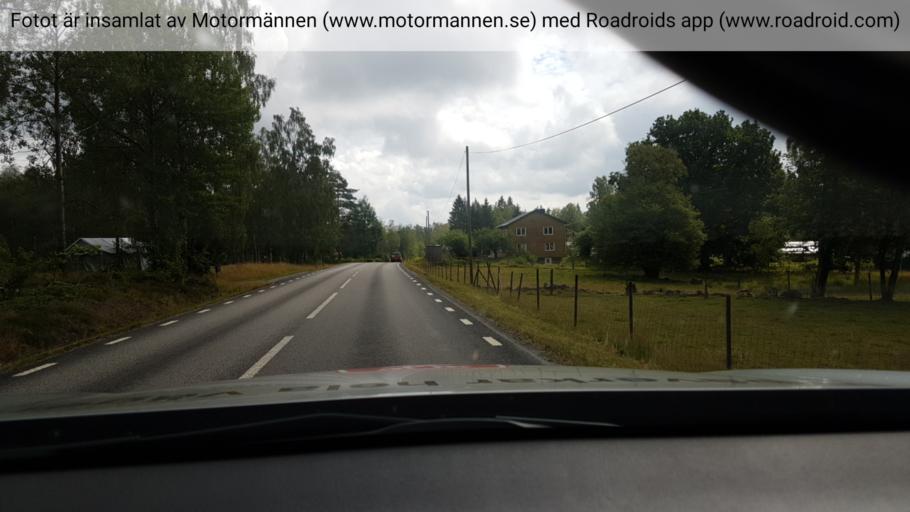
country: SE
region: Vaestra Goetaland
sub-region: Svenljunga Kommun
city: Svenljunga
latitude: 57.4846
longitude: 13.1406
